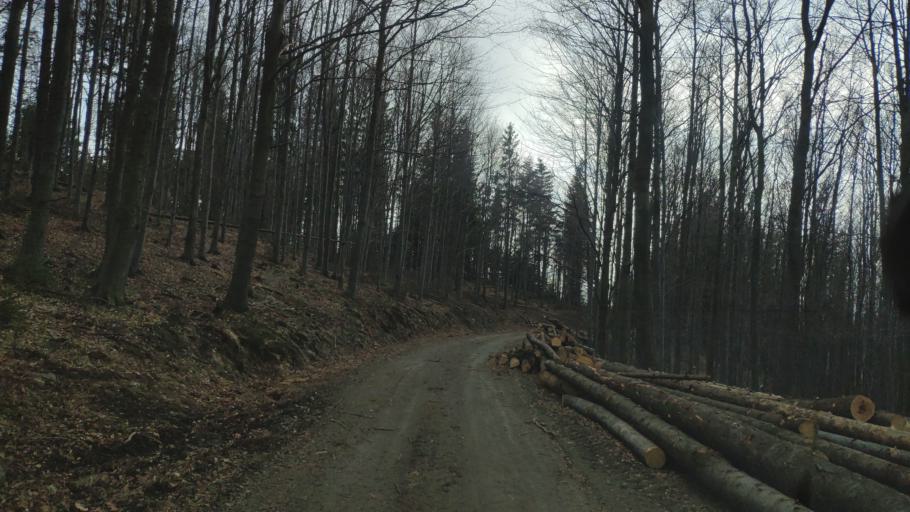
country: SK
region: Kosicky
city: Moldava nad Bodvou
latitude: 48.7493
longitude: 21.0407
